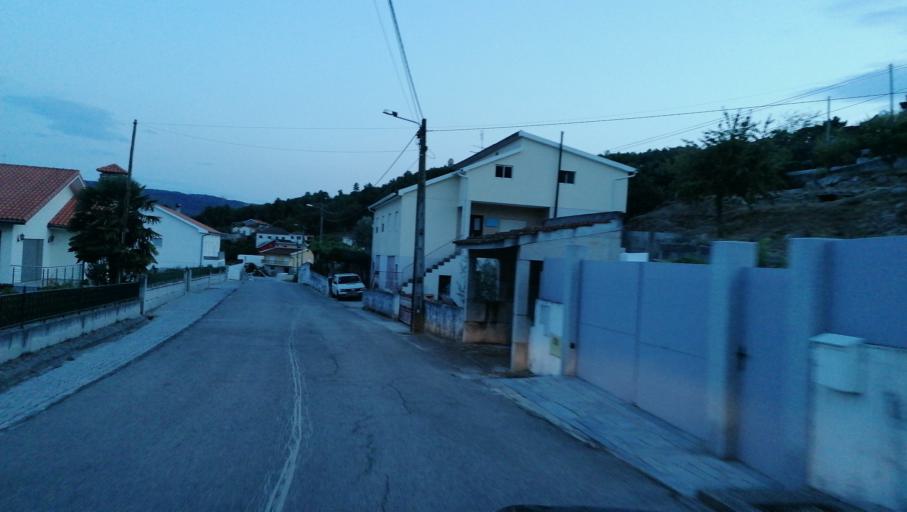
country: PT
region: Vila Real
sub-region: Vila Pouca de Aguiar
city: Vila Pouca de Aguiar
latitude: 41.5533
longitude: -7.6231
